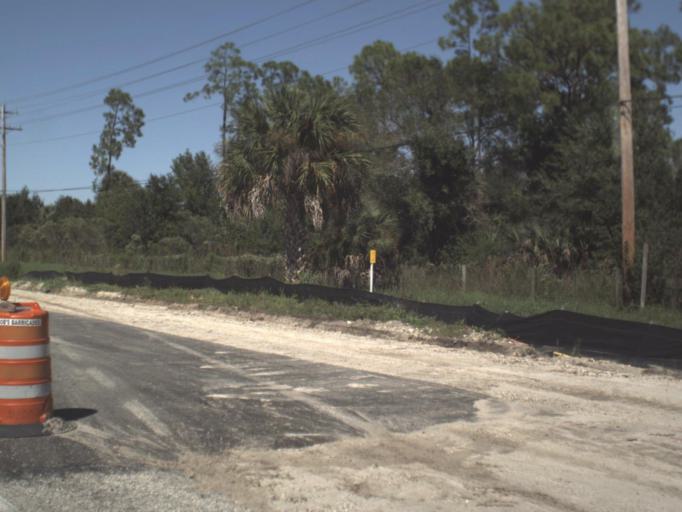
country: US
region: Florida
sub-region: Lee County
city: Suncoast Estates
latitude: 26.7309
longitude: -81.9095
